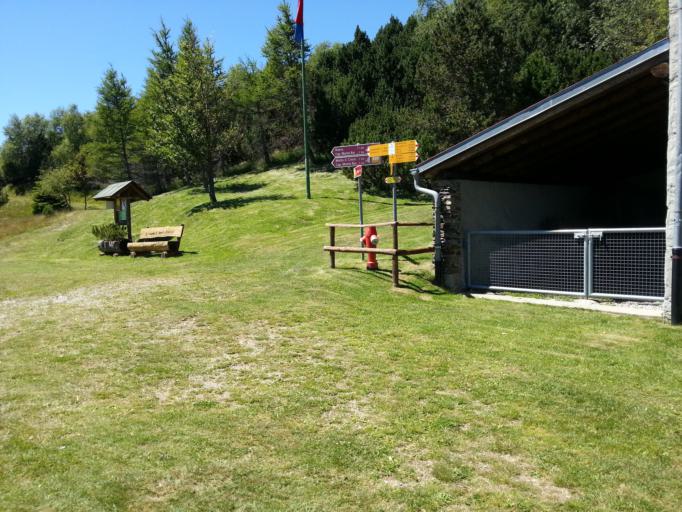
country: CH
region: Ticino
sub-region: Bellinzona District
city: Camorino
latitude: 46.1105
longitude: 9.0263
